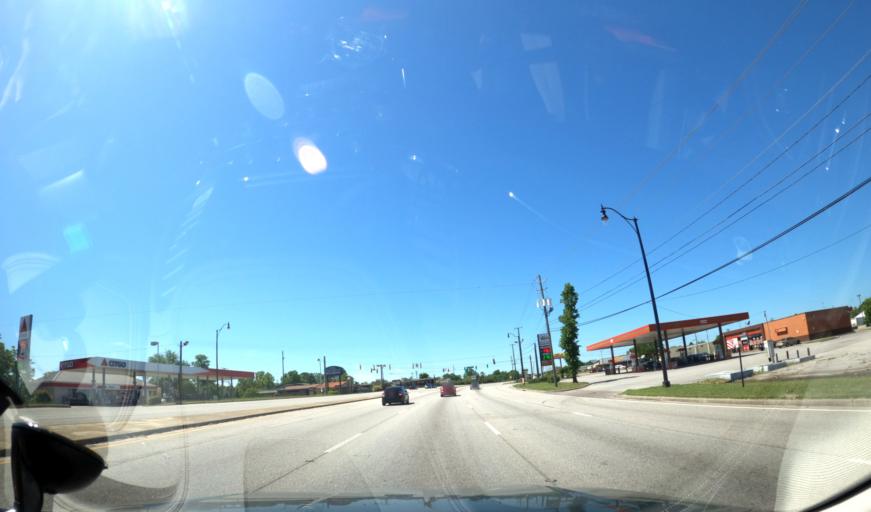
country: US
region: Georgia
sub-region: Richmond County
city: Augusta
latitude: 33.4567
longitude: -81.9682
